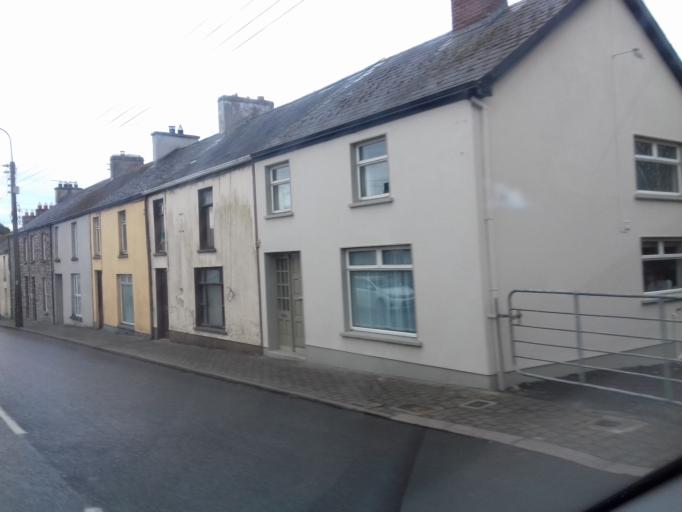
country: IE
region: Ulster
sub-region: An Cabhan
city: Ballyconnell
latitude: 54.1169
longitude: -7.5854
